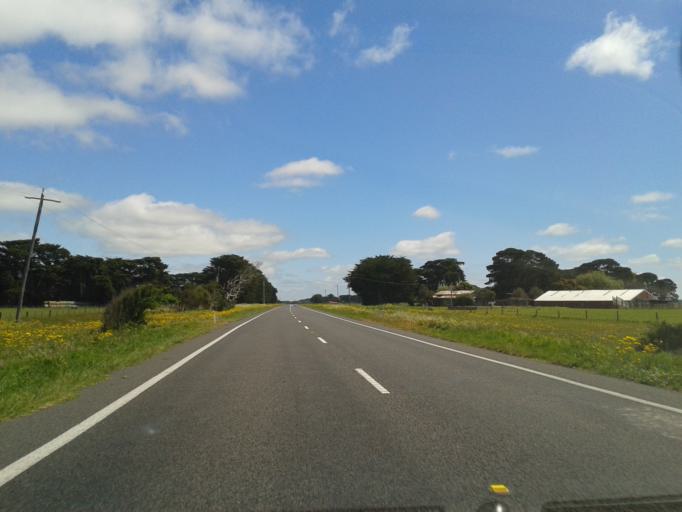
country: AU
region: Victoria
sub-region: Moyne
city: Port Fairy
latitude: -38.3367
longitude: 142.0965
